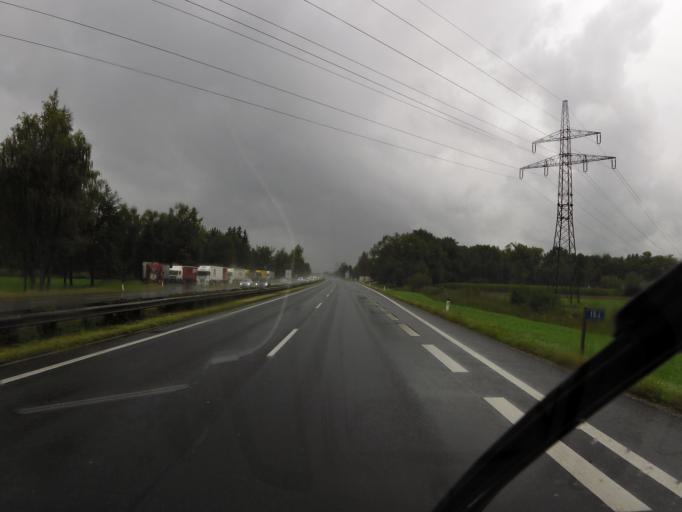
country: AT
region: Vorarlberg
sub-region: Politischer Bezirk Dornbirn
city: Dornbirn
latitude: 47.4338
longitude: 9.7212
